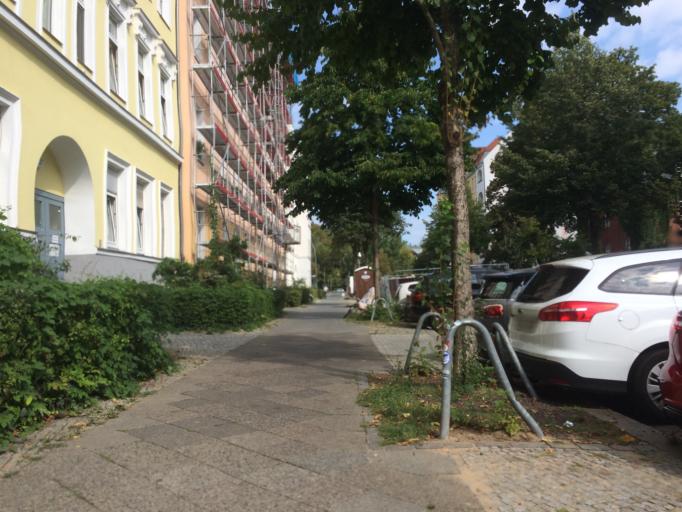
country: DE
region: Berlin
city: Wedding Bezirk
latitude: 52.5539
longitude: 13.3615
